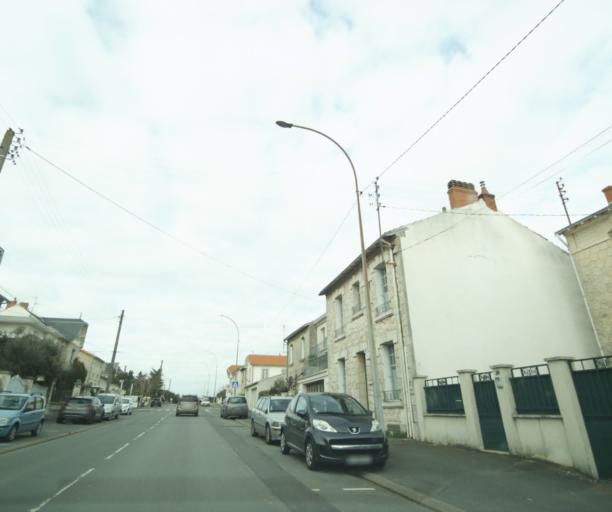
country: FR
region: Poitou-Charentes
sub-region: Departement de la Charente-Maritime
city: La Rochelle
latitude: 46.1643
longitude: -1.1648
